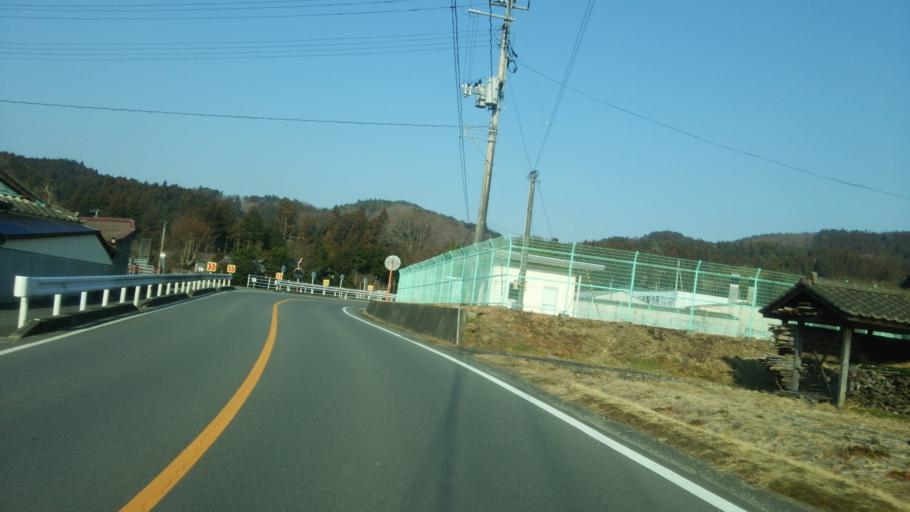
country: JP
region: Fukushima
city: Iwaki
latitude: 37.0752
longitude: 140.8032
